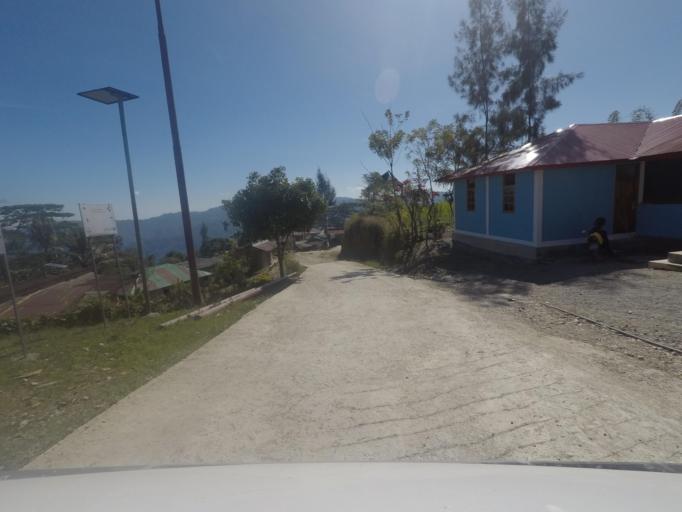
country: TL
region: Ermera
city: Gleno
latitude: -8.7296
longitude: 125.3409
